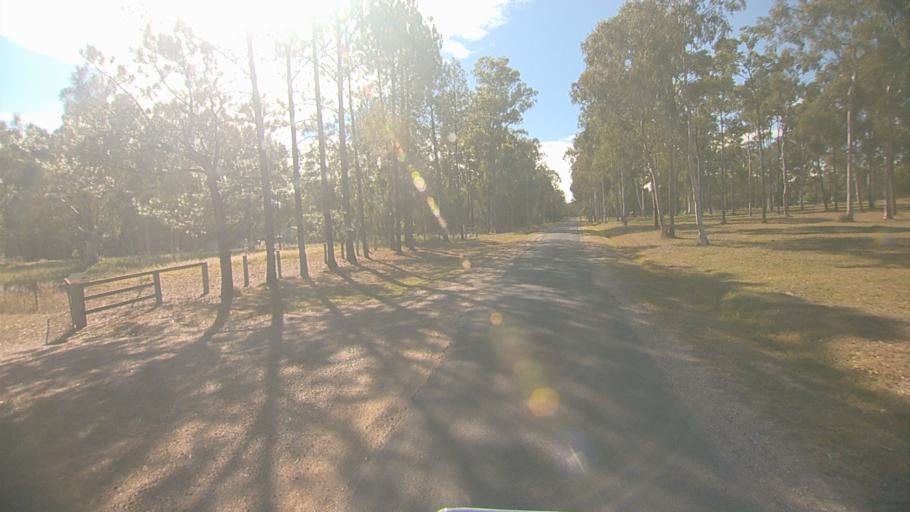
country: AU
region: Queensland
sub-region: Logan
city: Chambers Flat
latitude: -27.7866
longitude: 153.0691
